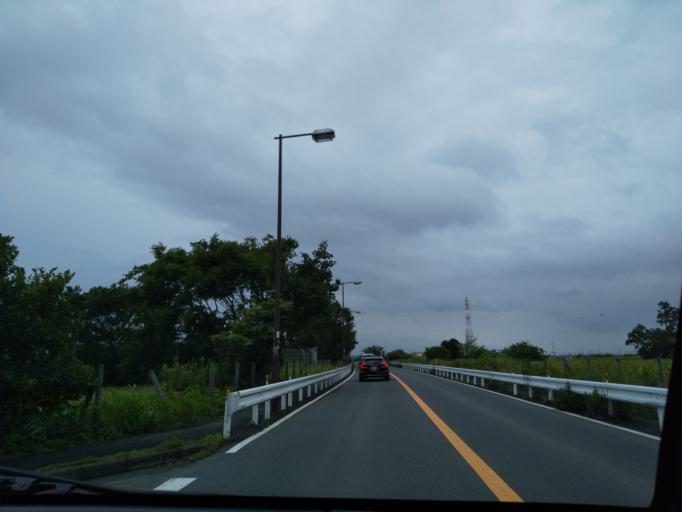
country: JP
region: Kanagawa
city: Fujisawa
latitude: 35.3982
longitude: 139.5037
